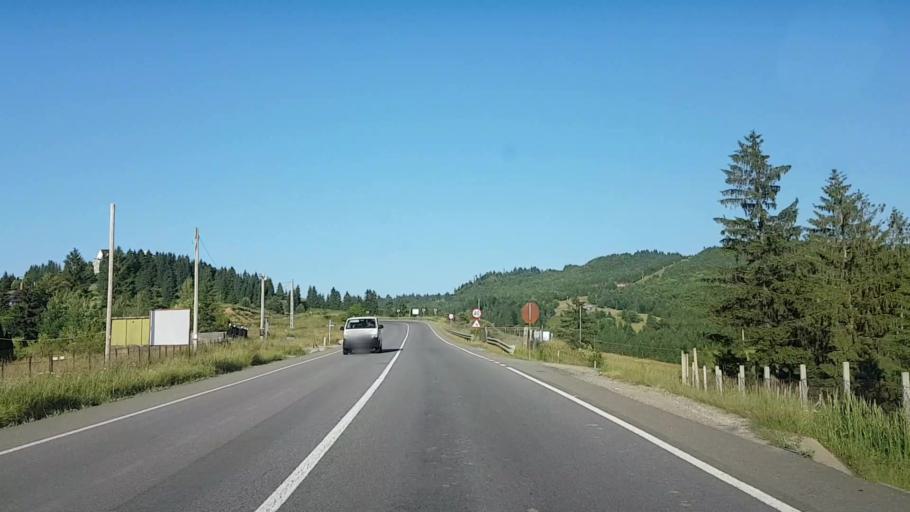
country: RO
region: Bistrita-Nasaud
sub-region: Comuna Lunca Ilvei
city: Lunca Ilvei
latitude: 47.2326
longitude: 24.9962
